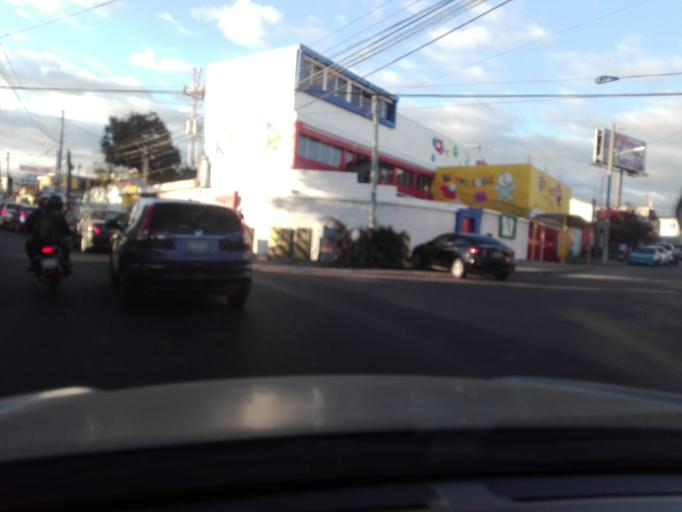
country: GT
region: Guatemala
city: Mixco
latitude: 14.5910
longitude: -90.5785
